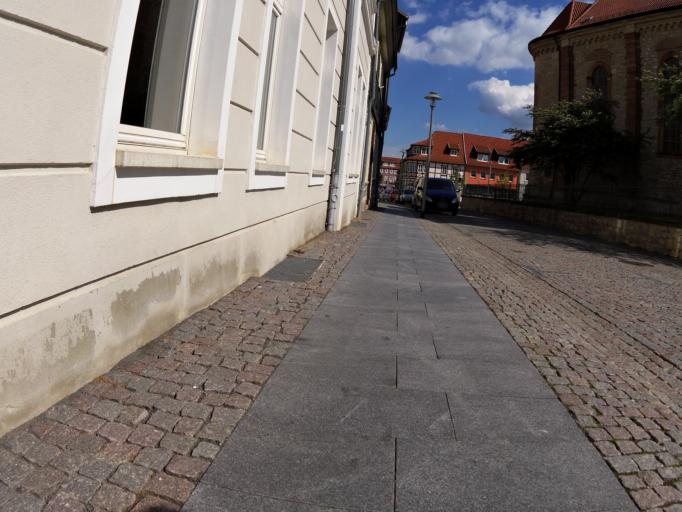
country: DE
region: Thuringia
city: Worbis
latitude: 51.4227
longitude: 10.3592
